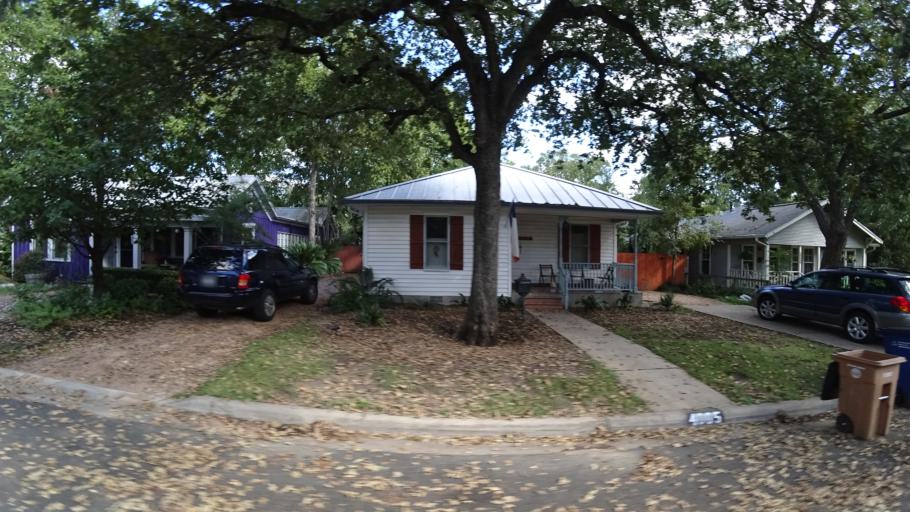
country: US
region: Texas
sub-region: Travis County
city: Austin
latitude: 30.3053
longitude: -97.7353
